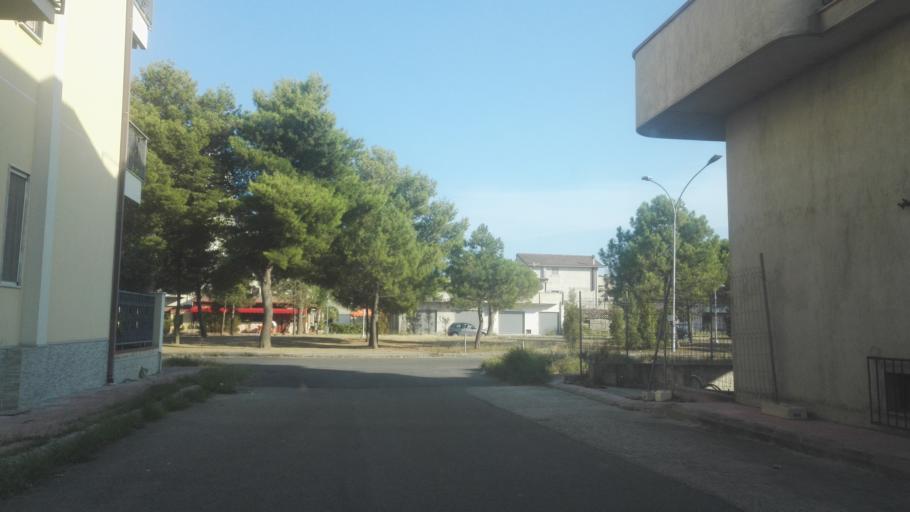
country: IT
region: Calabria
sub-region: Provincia di Reggio Calabria
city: Marina di Gioiosa Ionica
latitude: 38.3032
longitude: 16.3309
